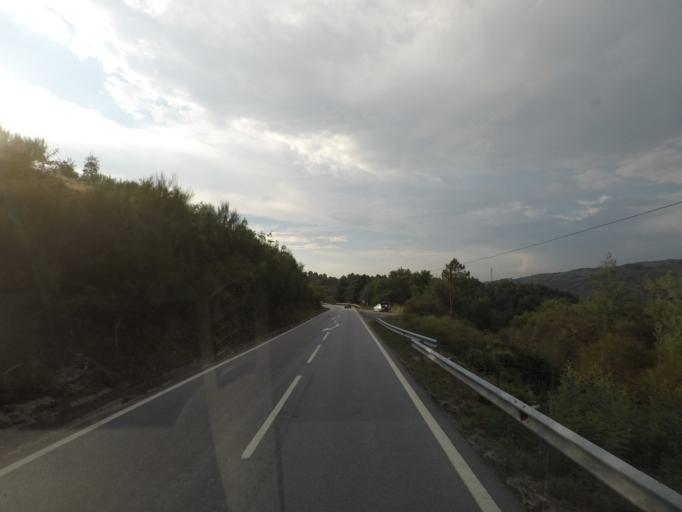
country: PT
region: Porto
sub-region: Baiao
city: Valadares
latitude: 41.2082
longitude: -7.9750
